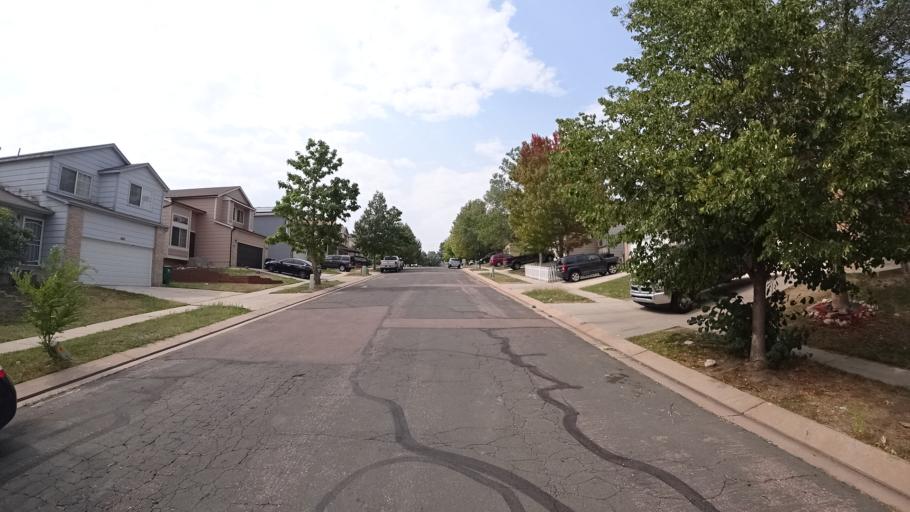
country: US
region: Colorado
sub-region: El Paso County
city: Cimarron Hills
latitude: 38.8228
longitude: -104.7450
